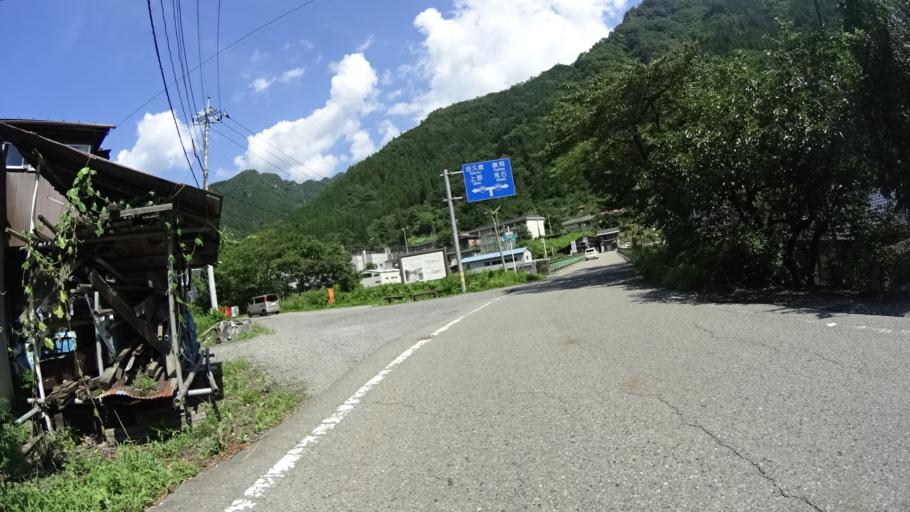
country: JP
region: Gunma
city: Tomioka
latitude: 36.0901
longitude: 138.8290
